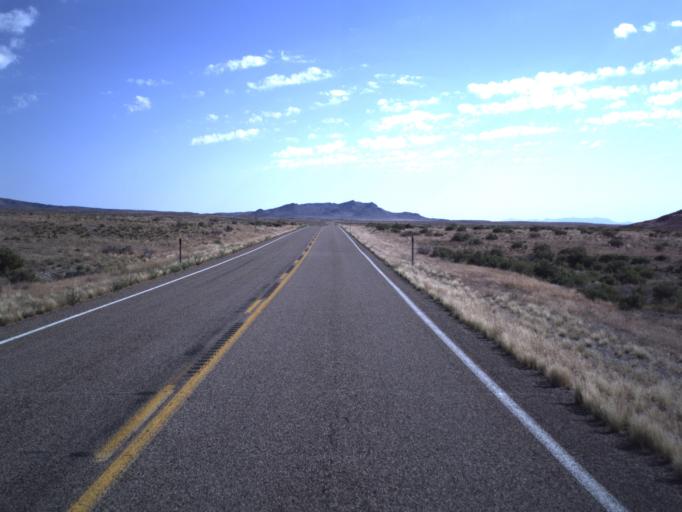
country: US
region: Utah
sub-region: Beaver County
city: Milford
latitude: 38.7478
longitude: -112.9514
